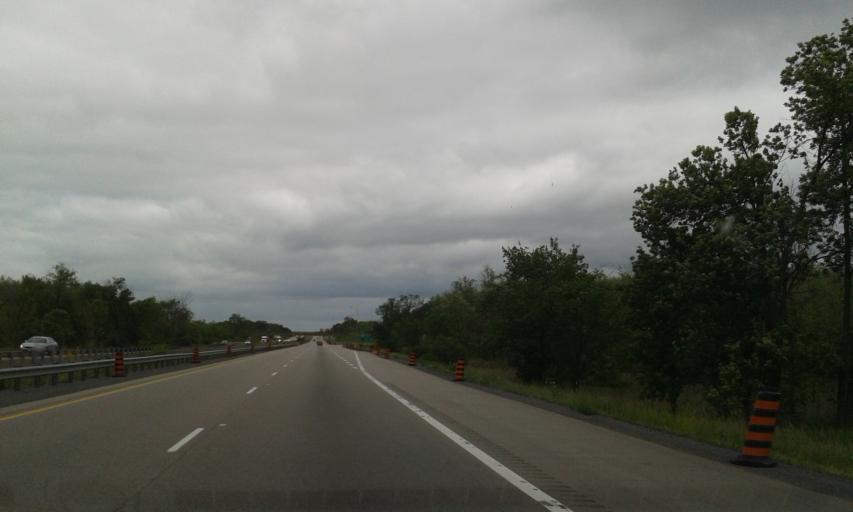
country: CA
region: Ontario
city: Skatepark
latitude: 44.2820
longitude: -76.7239
